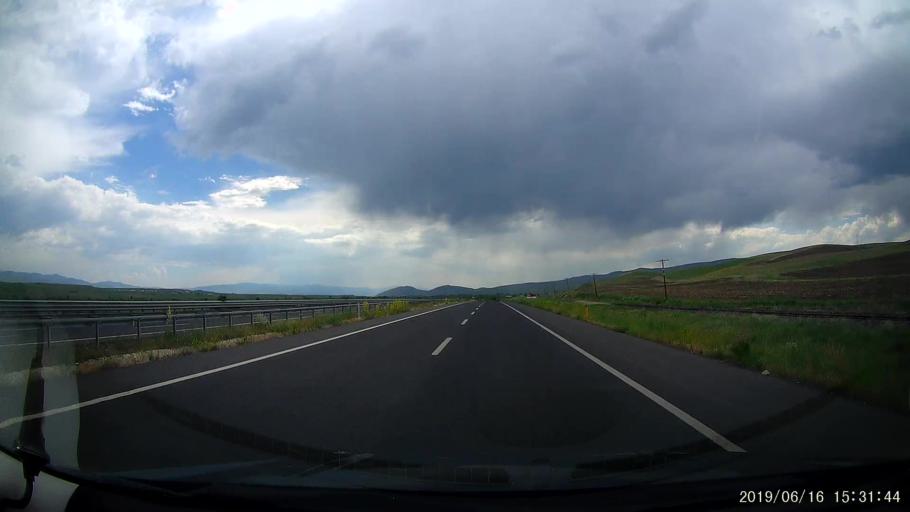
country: TR
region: Erzurum
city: Horasan
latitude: 40.0311
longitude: 42.0695
